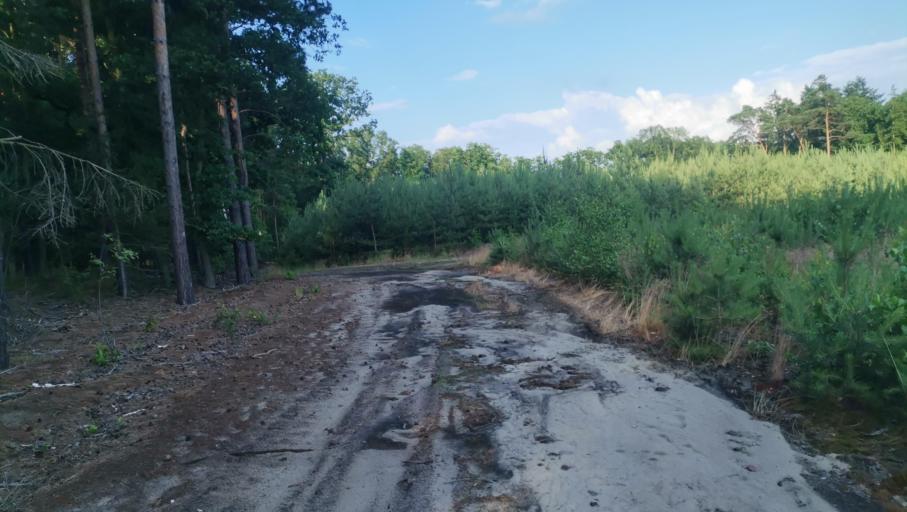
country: PL
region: Greater Poland Voivodeship
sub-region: Powiat jarocinski
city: Witaszyce
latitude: 51.9790
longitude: 17.5461
